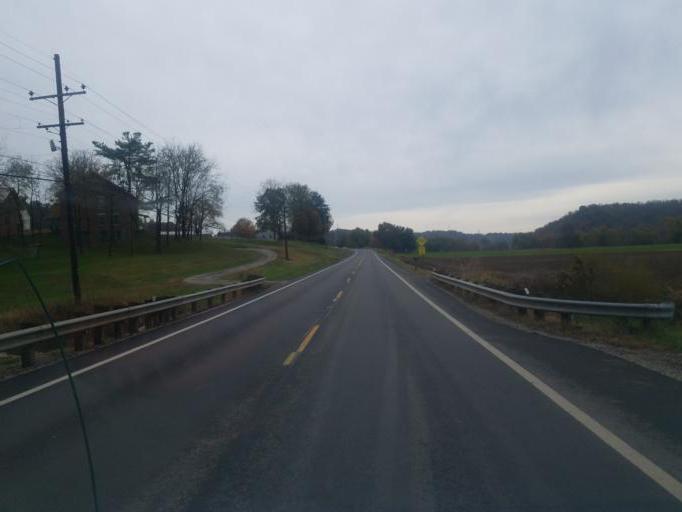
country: US
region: Ohio
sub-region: Washington County
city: Devola
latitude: 39.5242
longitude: -81.4953
